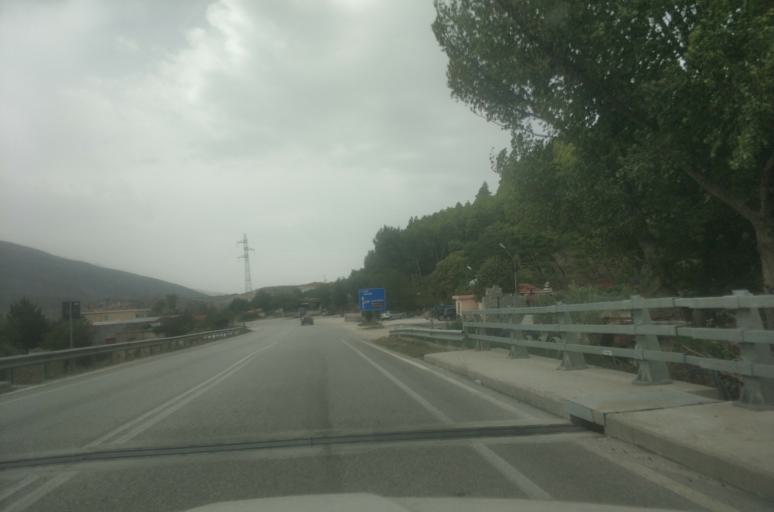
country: AL
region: Gjirokaster
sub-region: Rrethi i Tepelenes
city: Memaliaj
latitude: 40.3528
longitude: 19.9545
